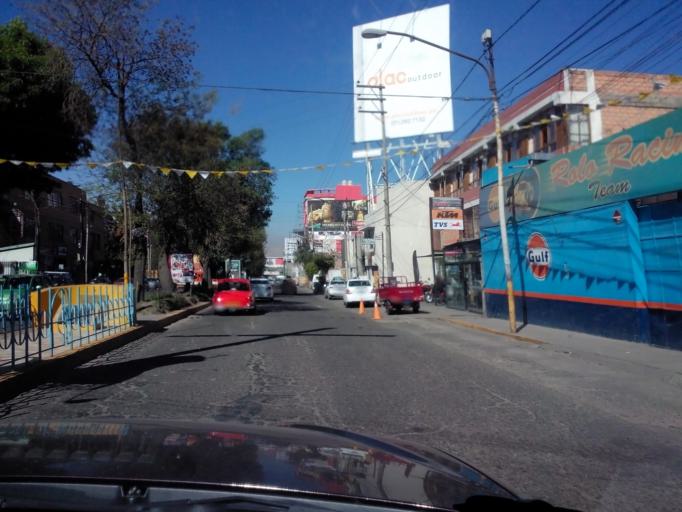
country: PE
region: Arequipa
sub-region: Provincia de Arequipa
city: Arequipa
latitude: -16.3885
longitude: -71.5512
